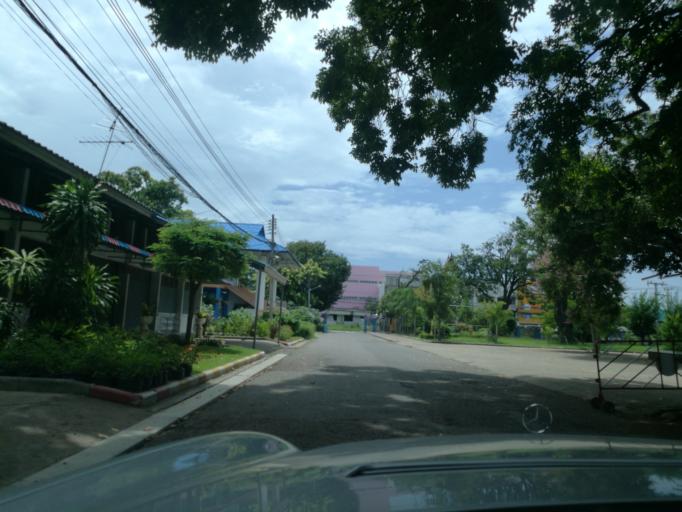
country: TH
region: Prachuap Khiri Khan
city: Prachuap Khiri Khan
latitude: 11.7993
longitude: 99.7981
